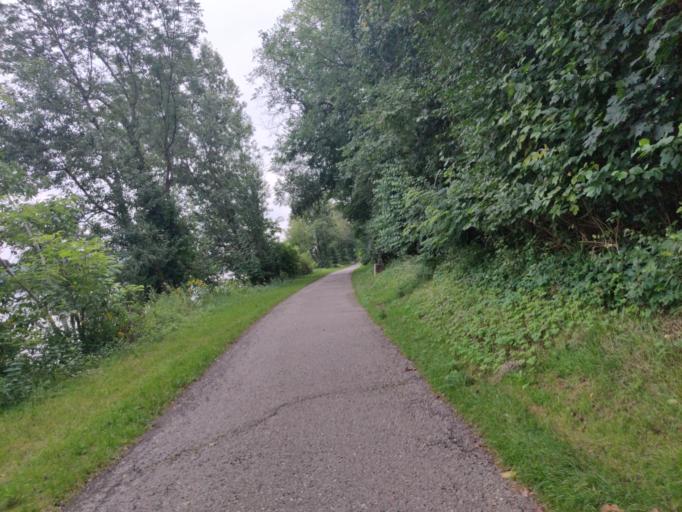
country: AT
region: Lower Austria
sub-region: Politischer Bezirk Tulln
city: Atzenbrugg
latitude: 48.3466
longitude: 15.9176
